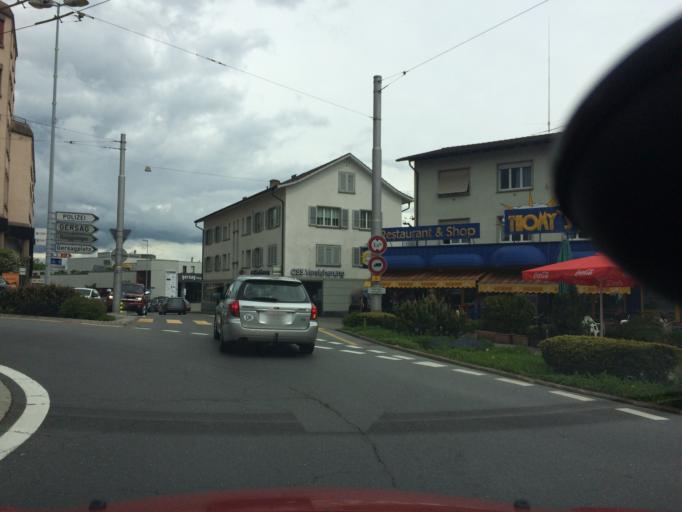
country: CH
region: Lucerne
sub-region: Hochdorf District
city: Emmen
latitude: 47.0772
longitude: 8.2757
